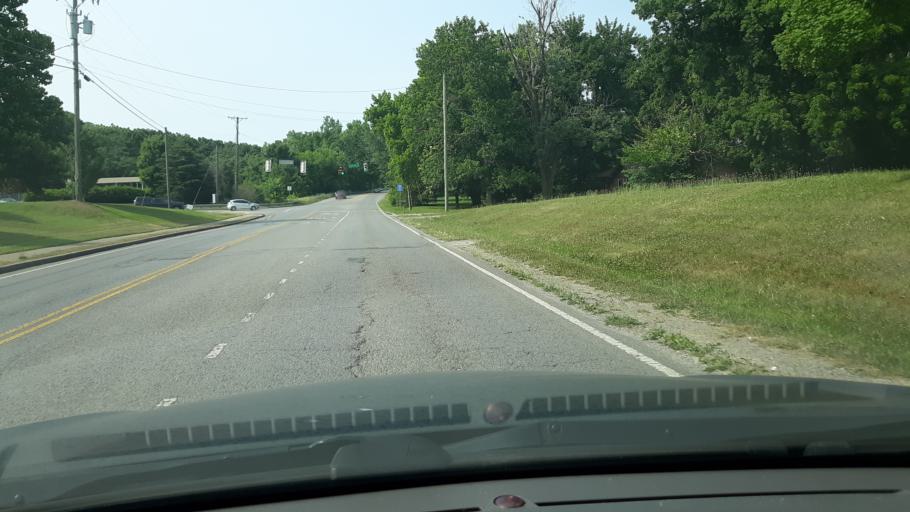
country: US
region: Tennessee
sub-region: Davidson County
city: Lakewood
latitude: 36.1771
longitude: -86.6139
